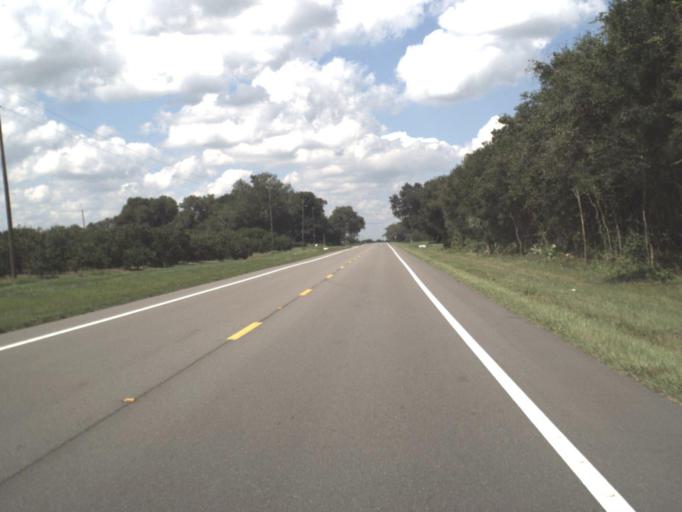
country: US
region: Florida
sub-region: Hardee County
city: Zolfo Springs
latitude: 27.4777
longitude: -81.7208
